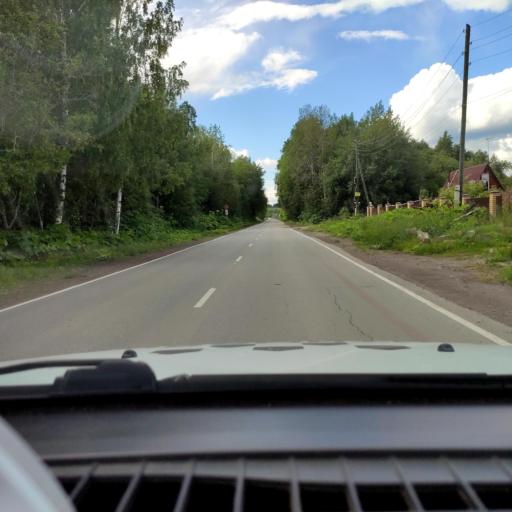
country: RU
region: Perm
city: Overyata
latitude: 58.1109
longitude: 55.8382
